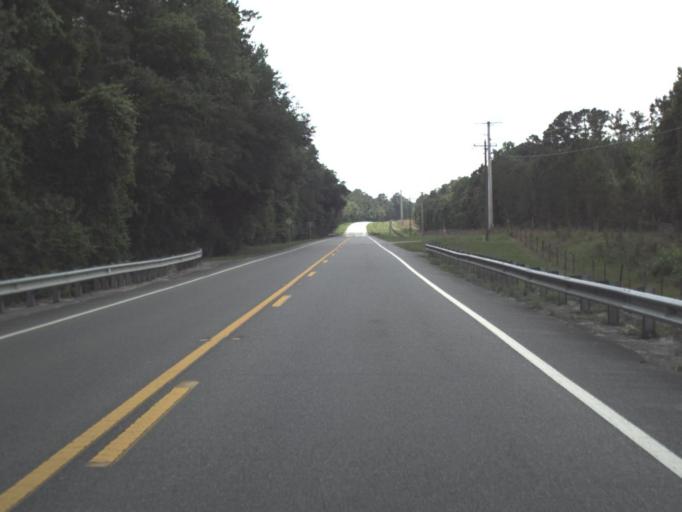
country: US
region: Florida
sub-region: Clay County
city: Asbury Lake
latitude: 29.9126
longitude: -81.8973
